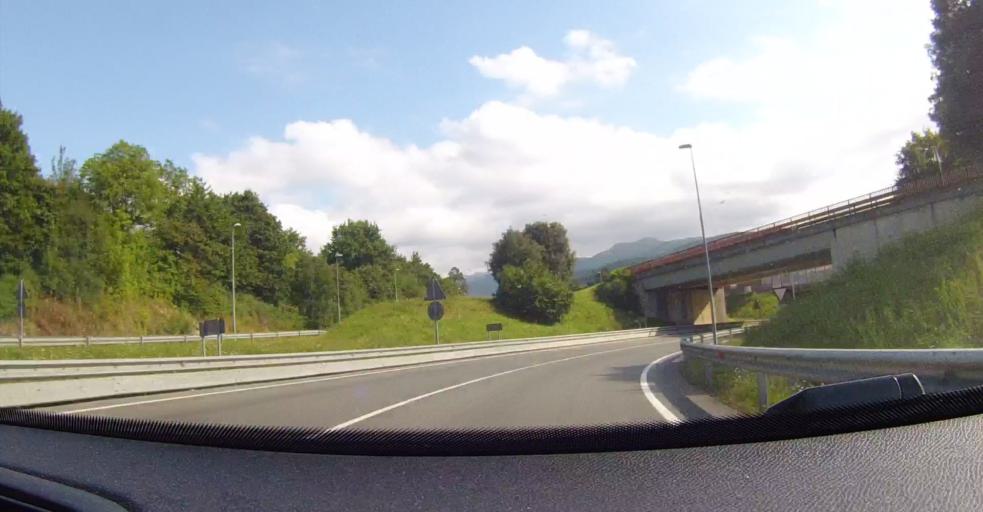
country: ES
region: Basque Country
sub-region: Bizkaia
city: Amorebieta
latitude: 43.2227
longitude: -2.7268
